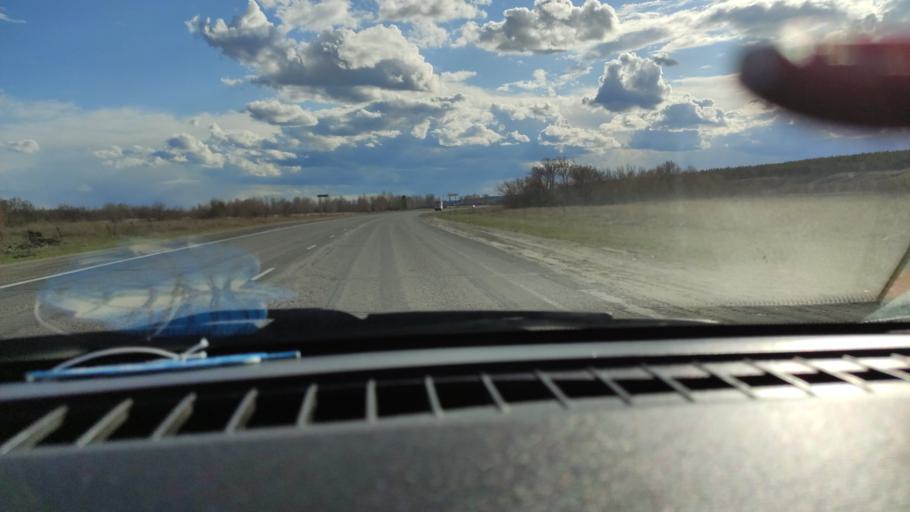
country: RU
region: Saratov
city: Sinodskoye
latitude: 52.0408
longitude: 46.7338
